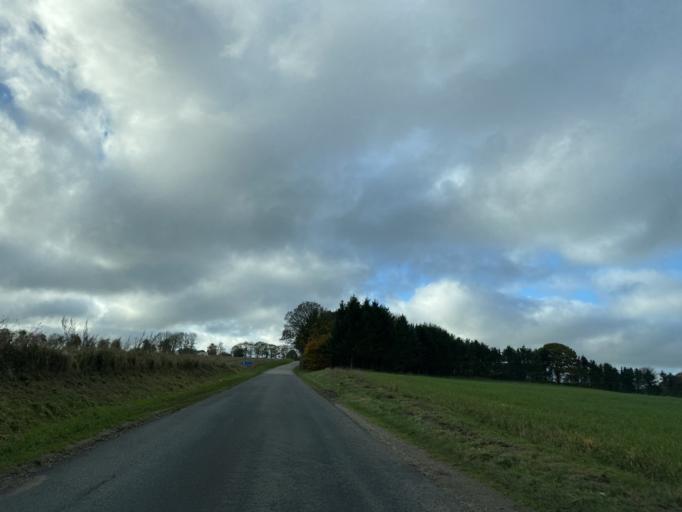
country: DK
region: Central Jutland
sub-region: Favrskov Kommune
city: Hammel
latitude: 56.2545
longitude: 9.7855
